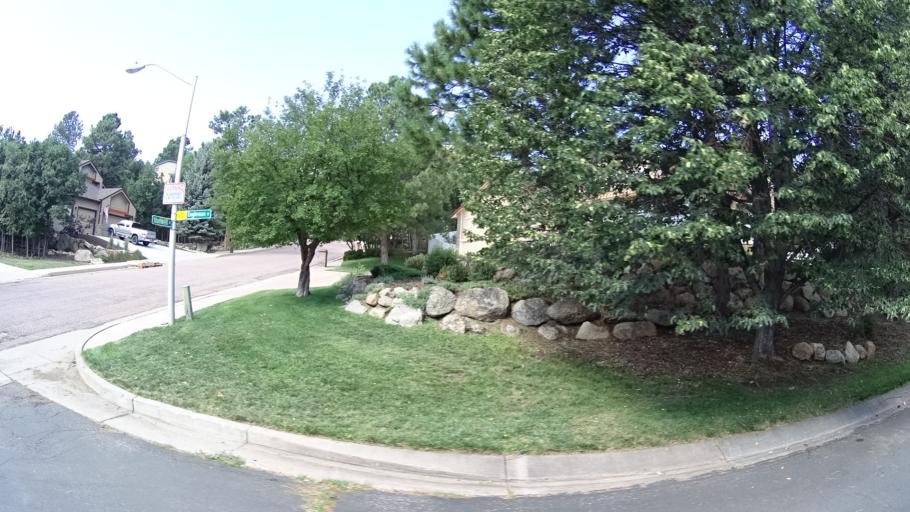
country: US
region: Colorado
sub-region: El Paso County
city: Fort Carson
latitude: 38.7572
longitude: -104.8327
